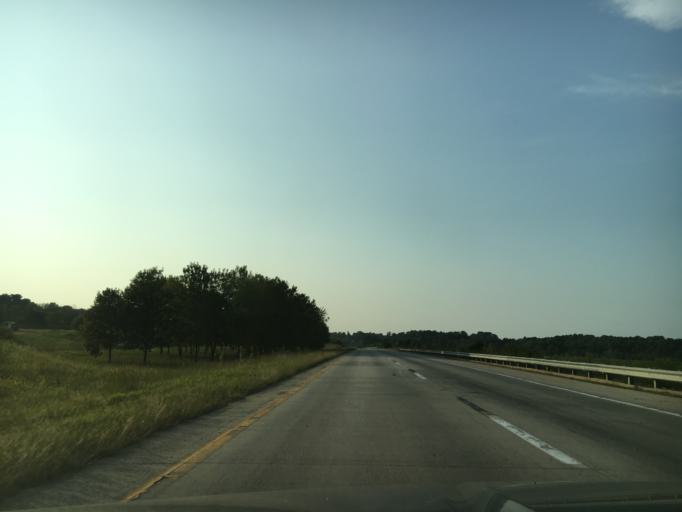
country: US
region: Virginia
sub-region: Appomattox County
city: Appomattox
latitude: 37.3475
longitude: -78.8068
